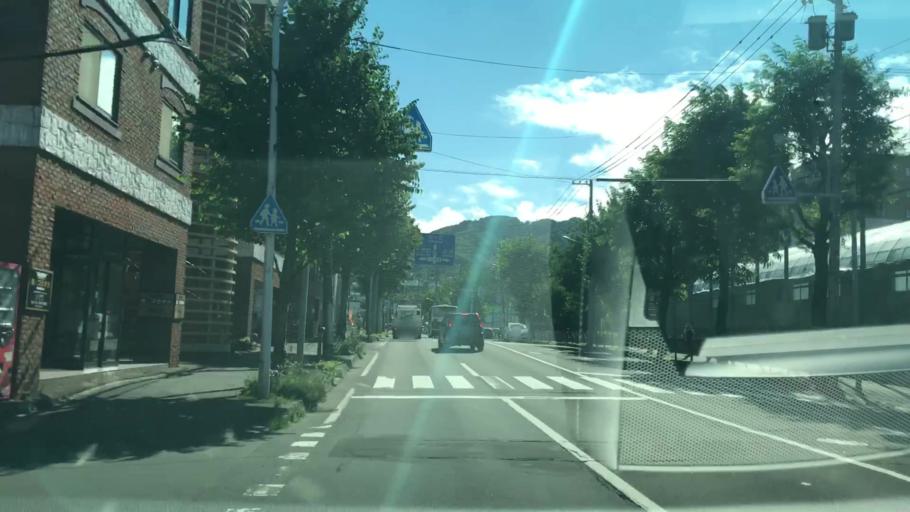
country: JP
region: Hokkaido
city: Sapporo
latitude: 43.0641
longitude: 141.3041
